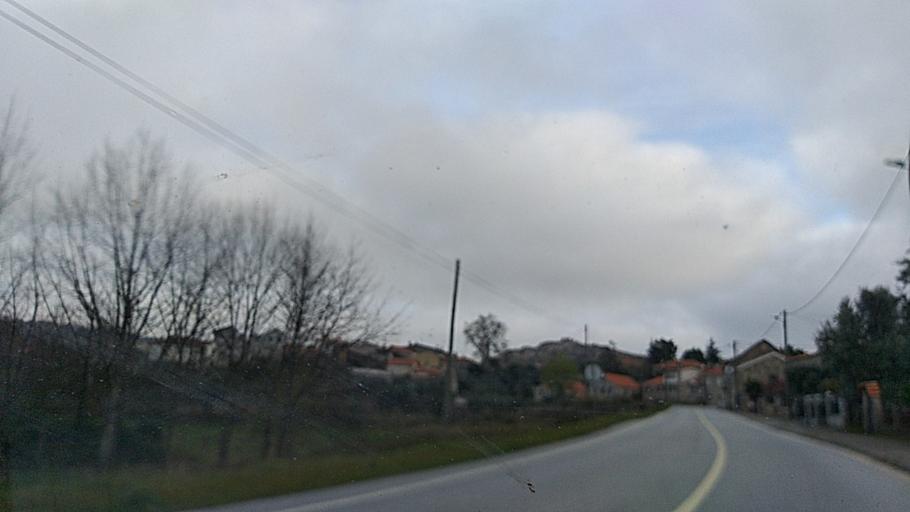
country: PT
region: Guarda
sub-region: Fornos de Algodres
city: Fornos de Algodres
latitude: 40.6534
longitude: -7.4864
